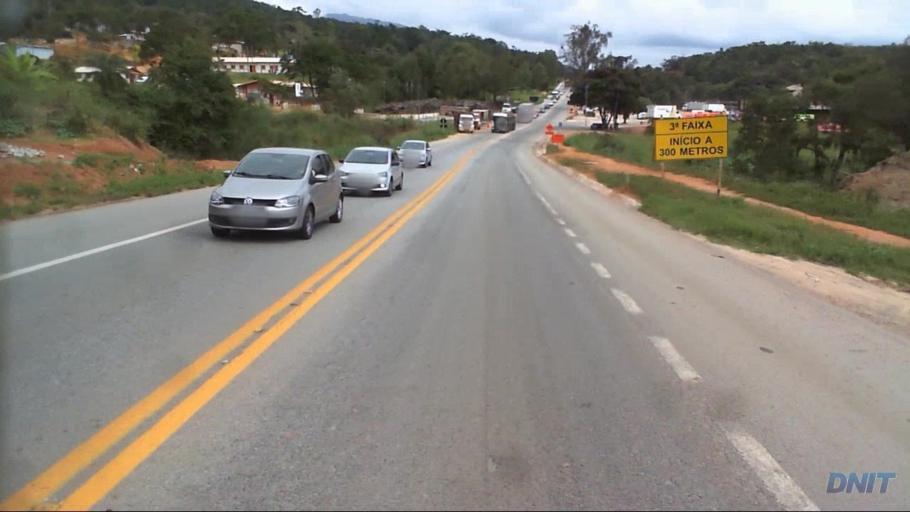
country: BR
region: Minas Gerais
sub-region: Caete
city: Caete
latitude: -19.7676
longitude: -43.6454
